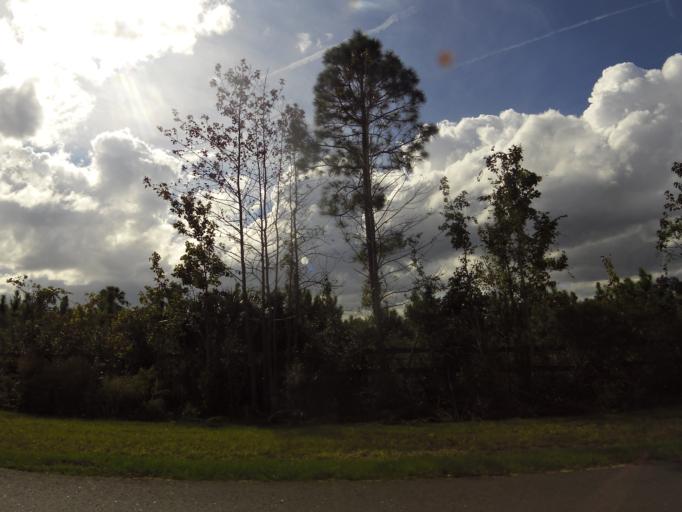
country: US
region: Florida
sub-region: Saint Johns County
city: Villano Beach
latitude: 29.9974
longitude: -81.3948
